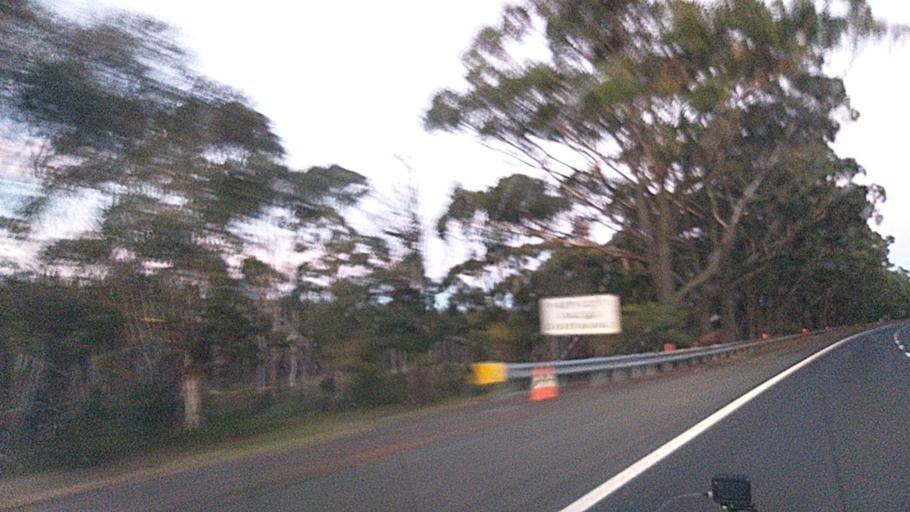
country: AU
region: New South Wales
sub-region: Wingecarribee
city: Bundanoon
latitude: -34.6293
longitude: 150.1958
